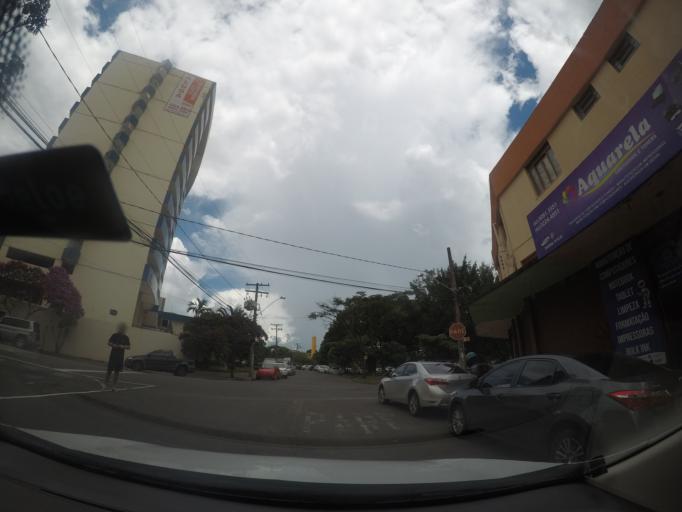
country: BR
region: Goias
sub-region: Goiania
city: Goiania
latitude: -16.6750
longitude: -49.2485
